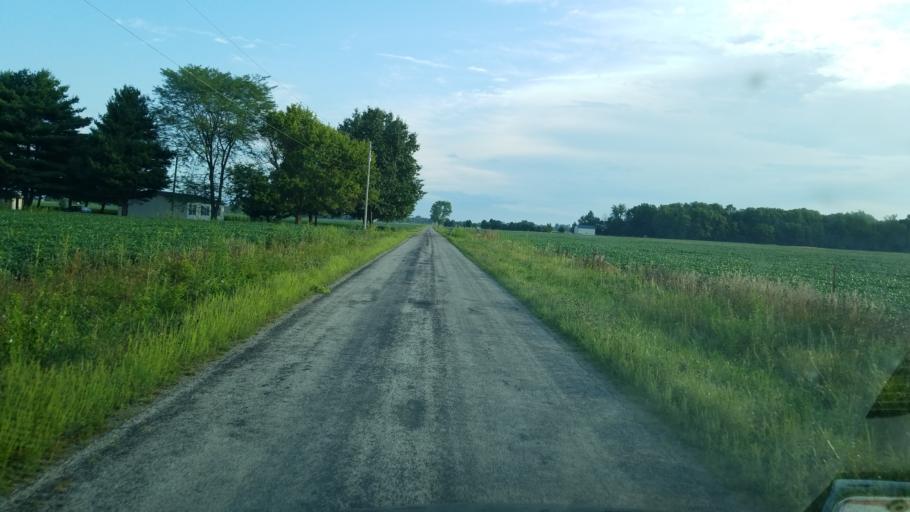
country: US
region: Ohio
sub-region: Morrow County
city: Mount Gilead
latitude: 40.6369
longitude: -82.8899
